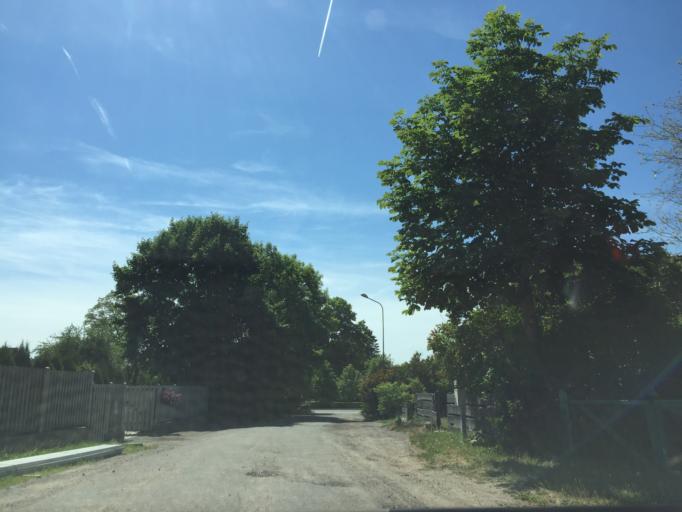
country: LV
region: Aizpute
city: Aizpute
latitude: 56.7126
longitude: 21.6182
